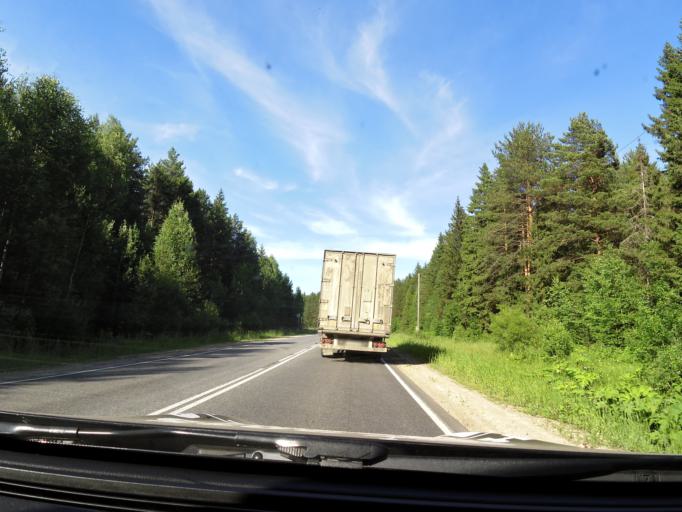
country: RU
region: Kirov
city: Belaya Kholunitsa
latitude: 58.8784
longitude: 50.8685
